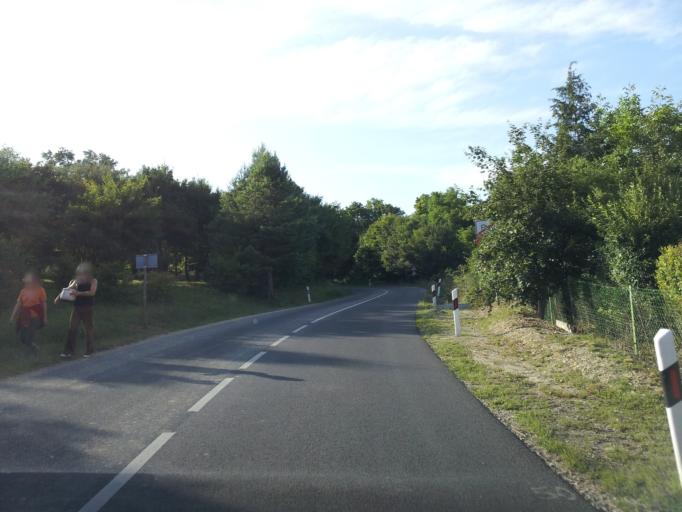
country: HU
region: Veszprem
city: Urkut
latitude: 46.9997
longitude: 17.6483
